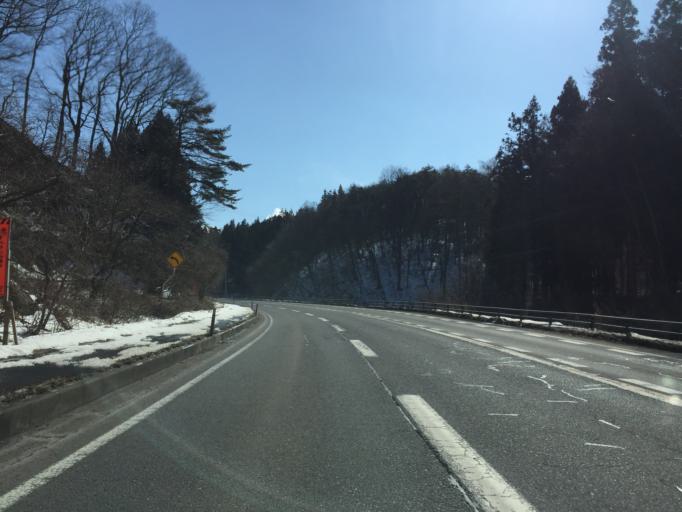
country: JP
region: Fukushima
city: Ishikawa
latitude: 37.2790
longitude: 140.5467
